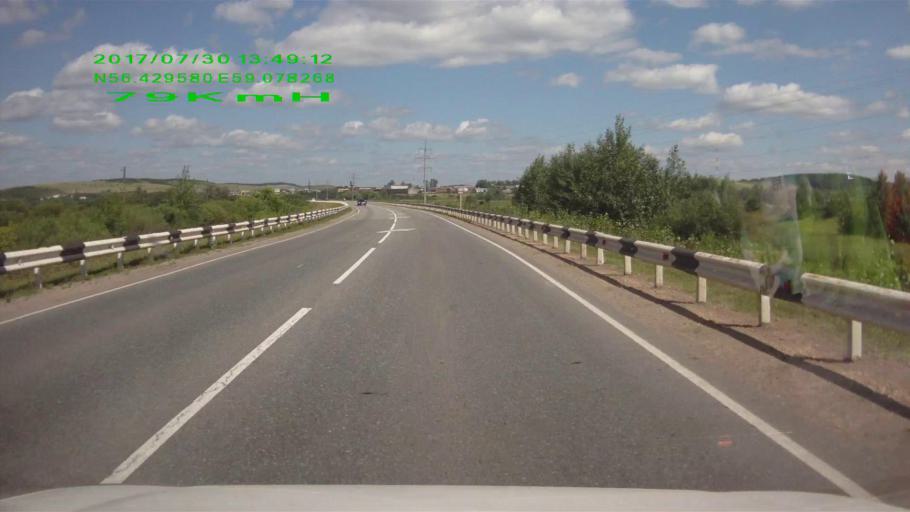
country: RU
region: Sverdlovsk
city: Mikhaylovsk
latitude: 56.4298
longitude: 59.0790
